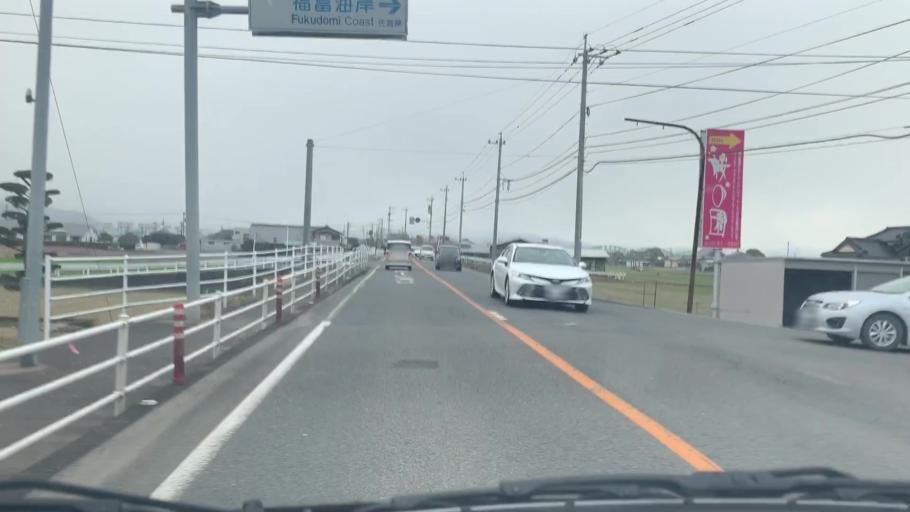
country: JP
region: Saga Prefecture
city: Saga-shi
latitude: 33.1932
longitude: 130.1929
